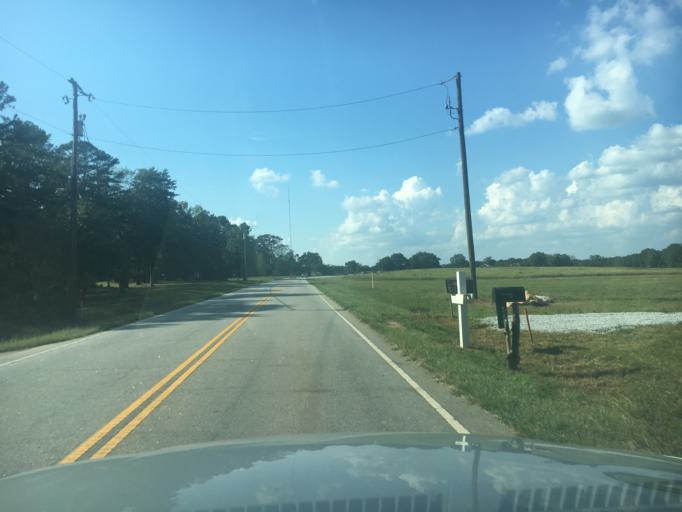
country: US
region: South Carolina
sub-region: Greenville County
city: Fountain Inn
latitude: 34.6350
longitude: -82.2556
